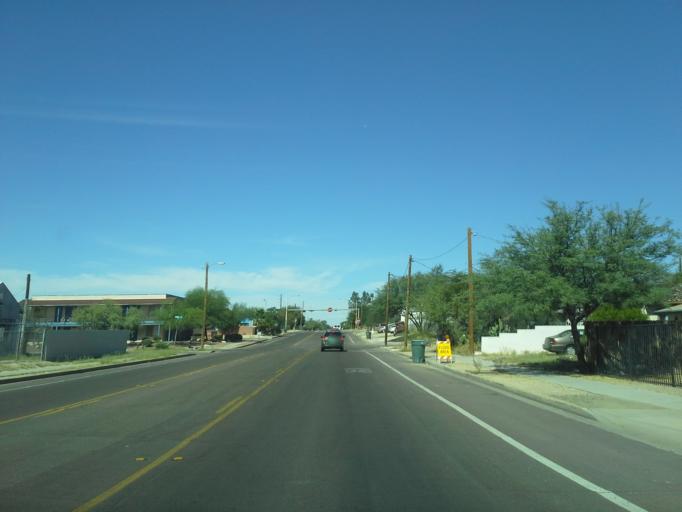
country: US
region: Arizona
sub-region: Pima County
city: South Tucson
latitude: 32.2378
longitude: -110.9687
